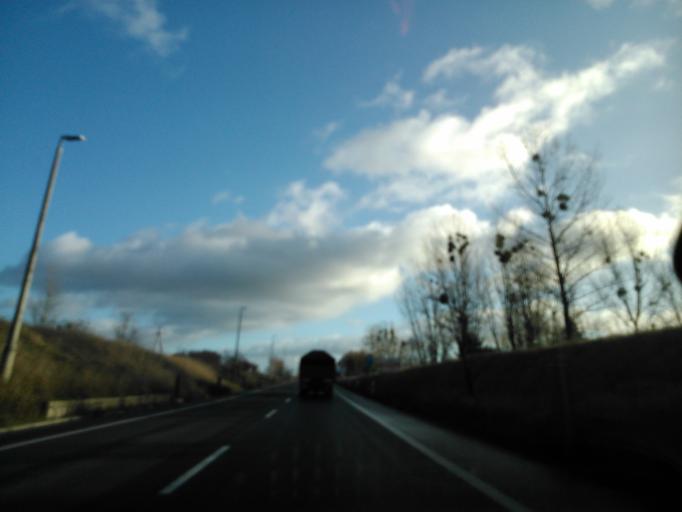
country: PL
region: Kujawsko-Pomorskie
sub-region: Powiat torunski
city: Wielka Nieszawka
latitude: 52.9758
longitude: 18.5546
